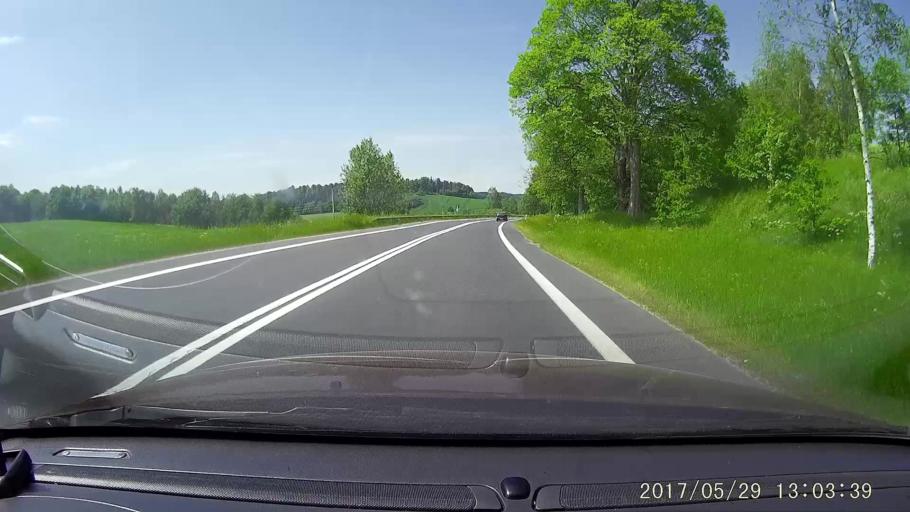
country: PL
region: Lower Silesian Voivodeship
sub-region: Powiat jeleniogorski
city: Stara Kamienica
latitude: 50.9241
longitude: 15.6098
